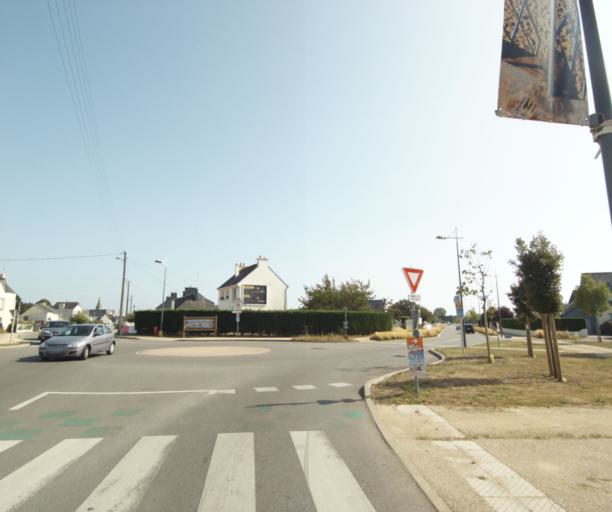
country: FR
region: Brittany
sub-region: Departement du Morbihan
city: Merlevenez
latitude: 47.7009
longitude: -3.2576
